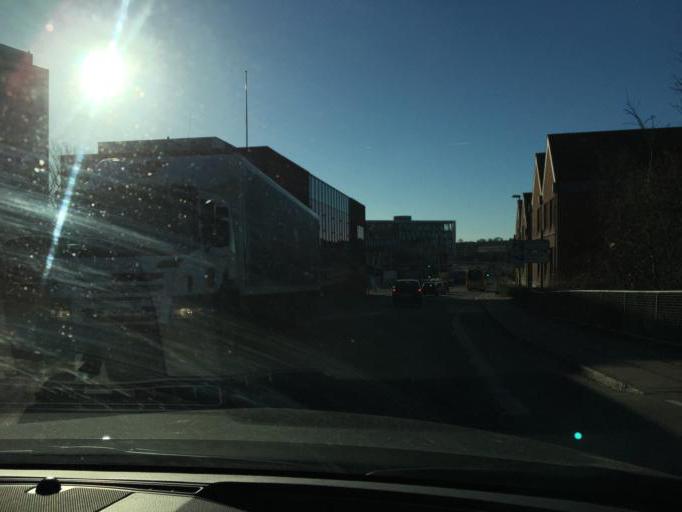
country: DK
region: South Denmark
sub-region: Kolding Kommune
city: Kolding
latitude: 55.4892
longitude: 9.4792
